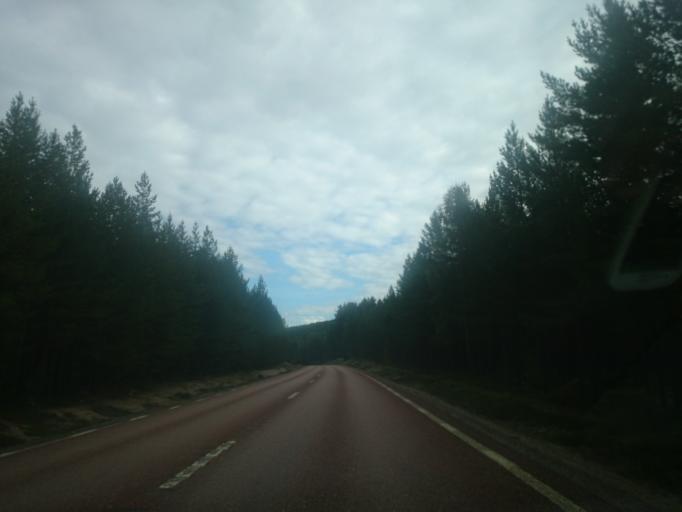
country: SE
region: Gaevleborg
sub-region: Ljusdals Kommun
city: Farila
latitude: 61.8898
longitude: 15.6696
